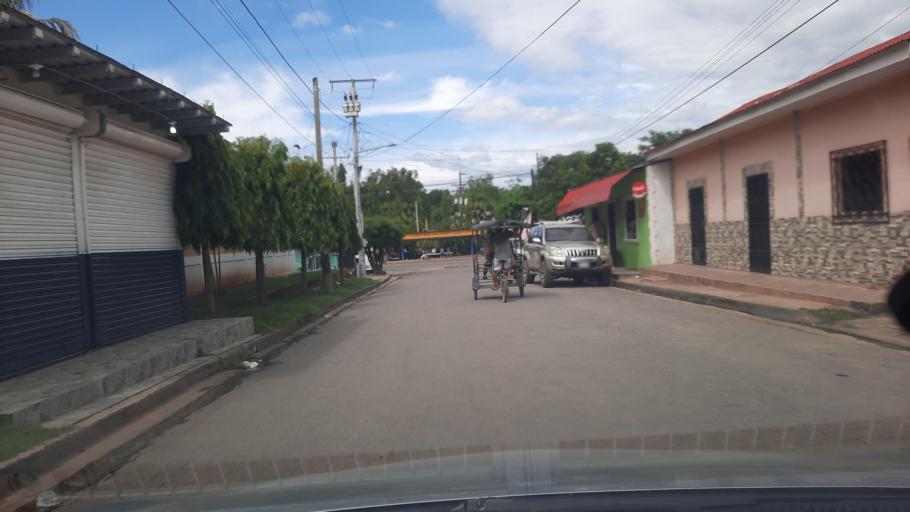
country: NI
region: Chinandega
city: Somotillo
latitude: 13.0452
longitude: -86.9033
